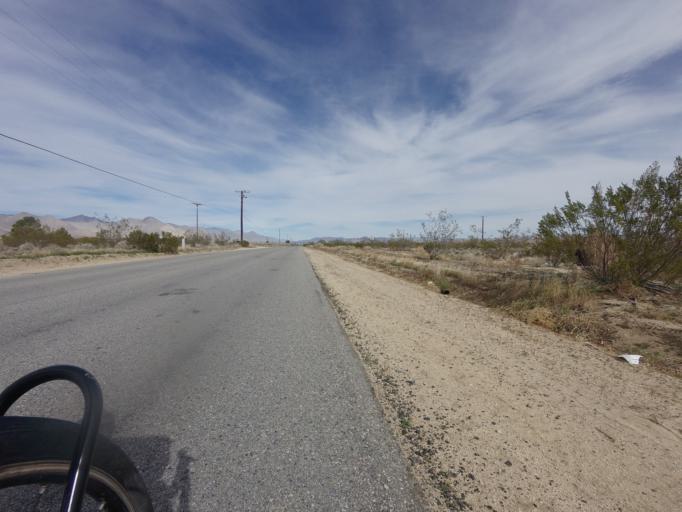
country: US
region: California
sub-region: Kern County
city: Inyokern
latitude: 35.7008
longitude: -117.8283
